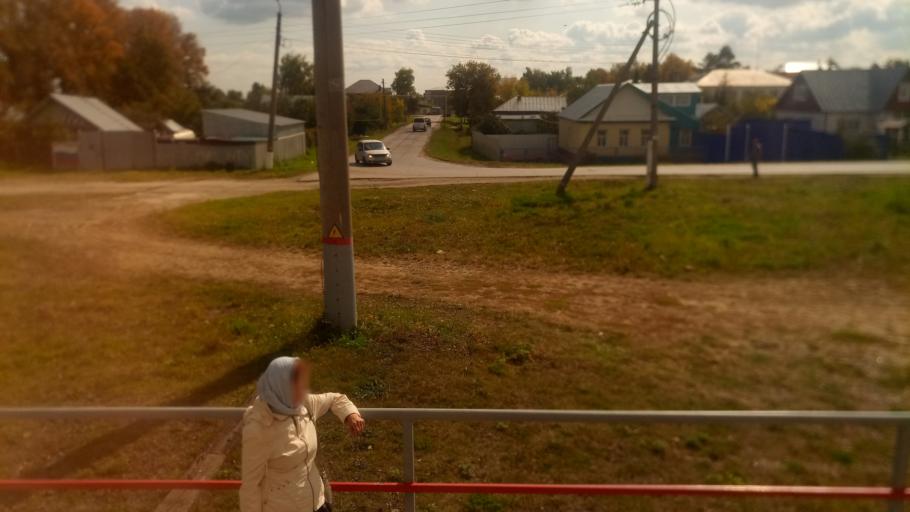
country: RU
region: Chuvashia
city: Urmary
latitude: 55.6868
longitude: 47.9453
